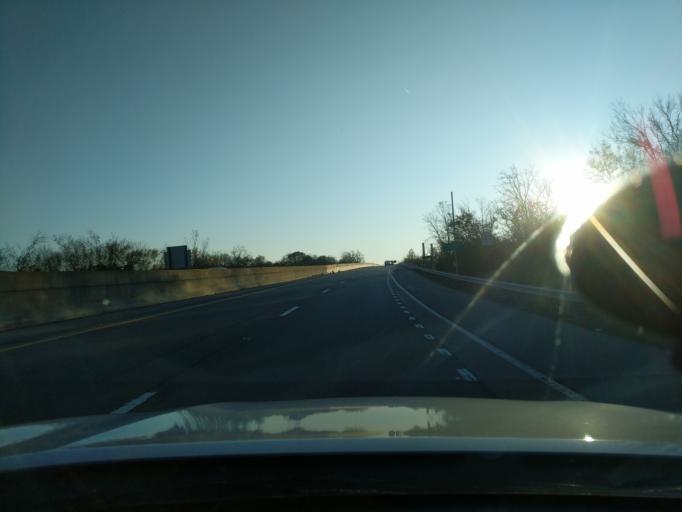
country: US
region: Tennessee
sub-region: Davidson County
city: Nashville
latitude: 36.1854
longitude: -86.8634
